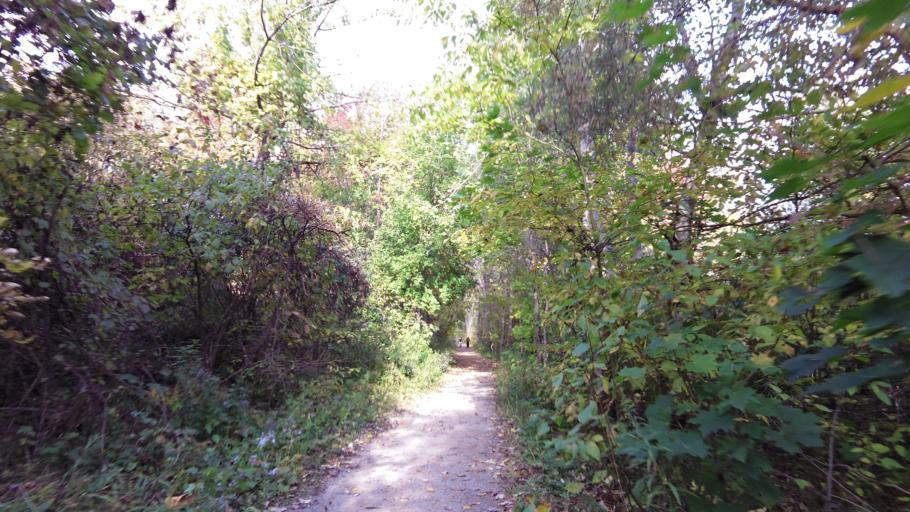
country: CA
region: Ontario
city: Orangeville
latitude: 43.8206
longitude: -80.0242
